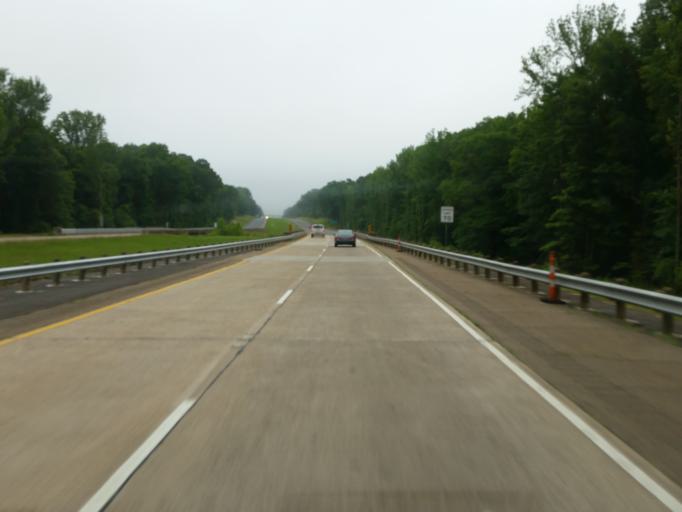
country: US
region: Louisiana
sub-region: Webster Parish
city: Minden
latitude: 32.5617
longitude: -93.1502
